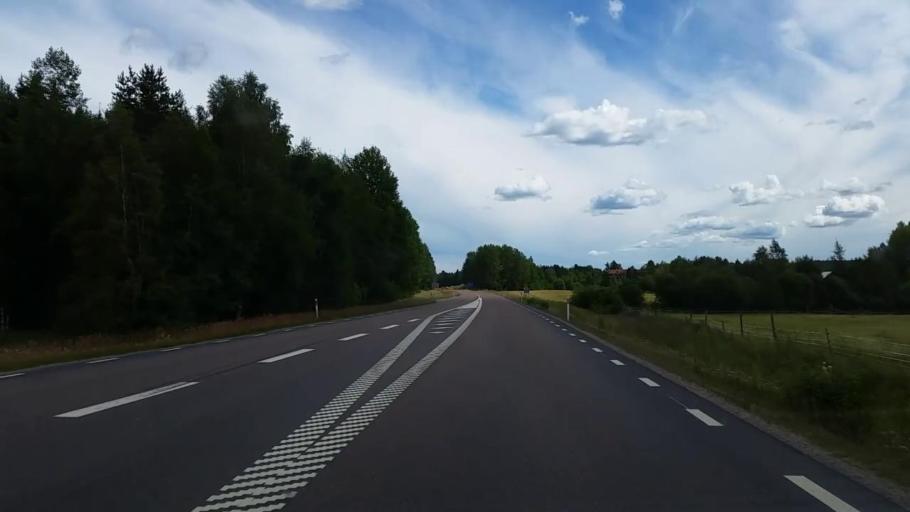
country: SE
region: Gaevleborg
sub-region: Ovanakers Kommun
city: Edsbyn
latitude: 61.3717
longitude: 15.8500
